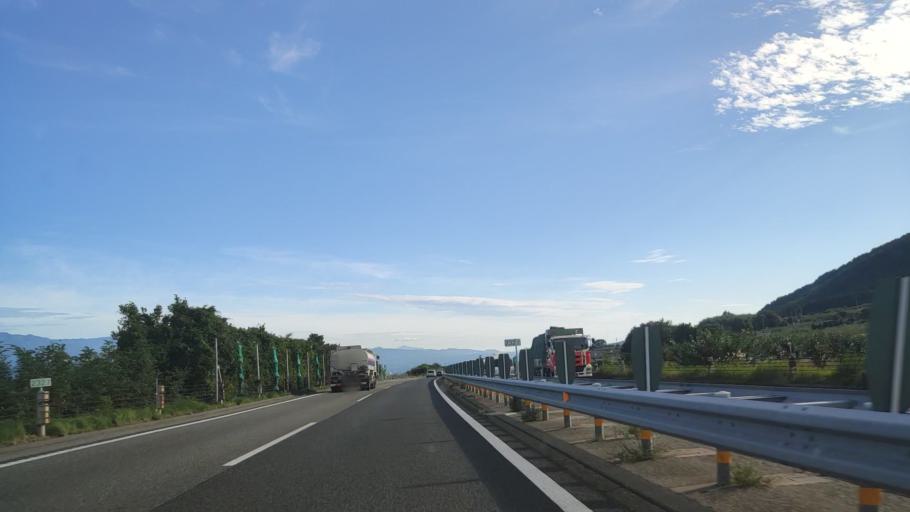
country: JP
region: Nagano
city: Iida
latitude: 35.6358
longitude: 137.8957
